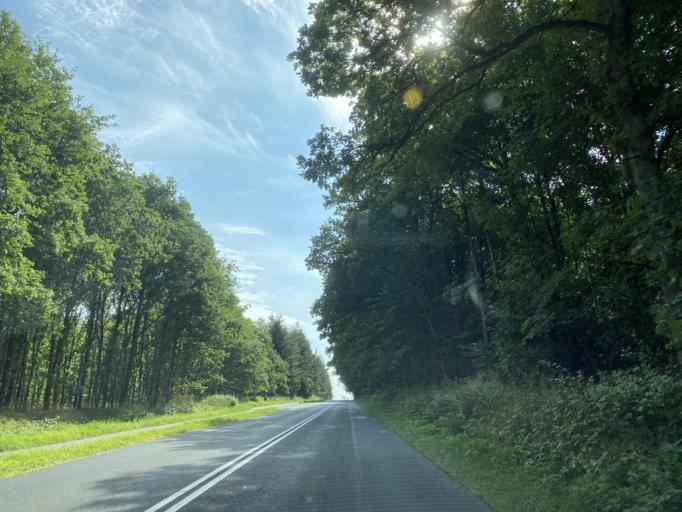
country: DK
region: Central Jutland
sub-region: Favrskov Kommune
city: Hammel
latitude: 56.2636
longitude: 9.8437
